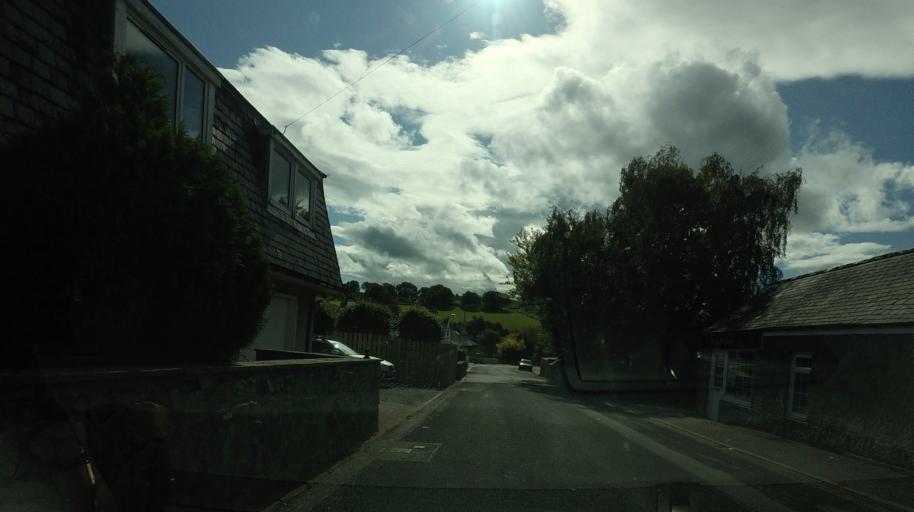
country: GB
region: Scotland
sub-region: Aberdeenshire
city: Torphins
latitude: 57.1295
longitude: -2.6890
